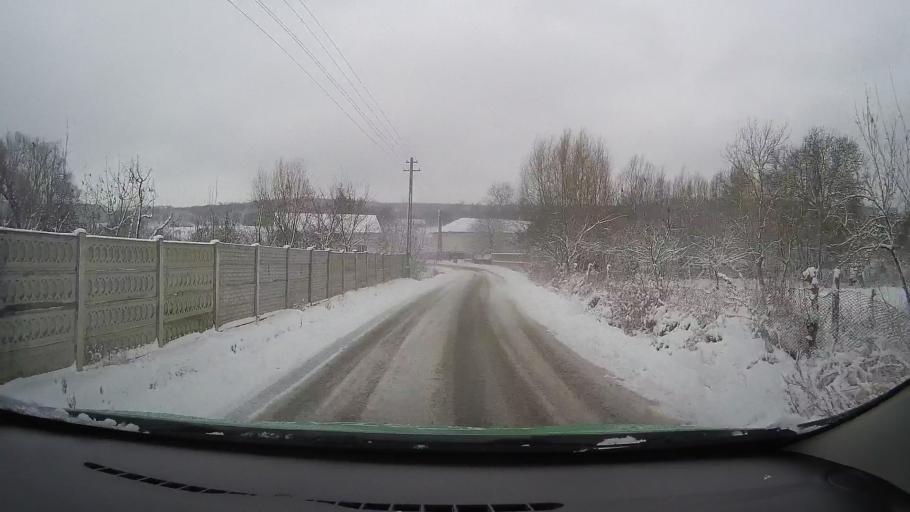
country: RO
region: Hunedoara
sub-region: Comuna Pestisu Mic
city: Pestisu Mic
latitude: 45.8180
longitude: 22.8932
